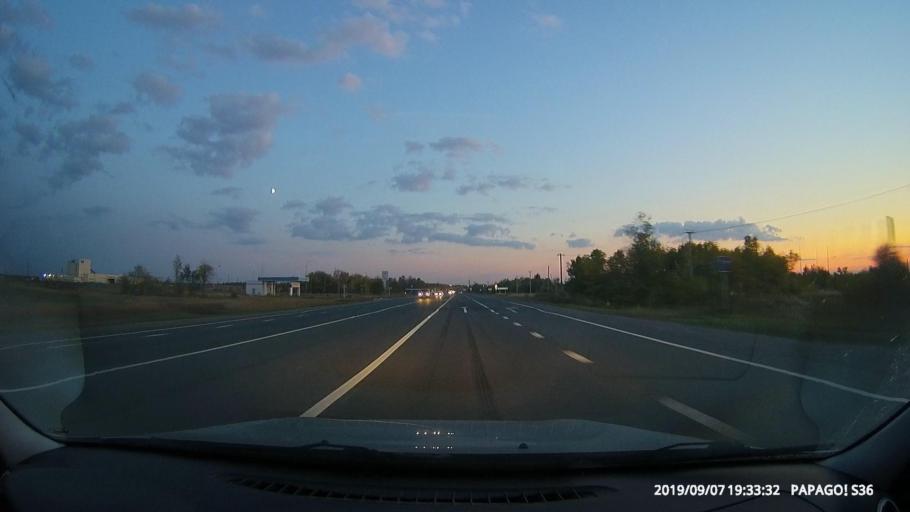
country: RU
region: Samara
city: Chapayevsk
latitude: 52.9964
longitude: 49.7750
